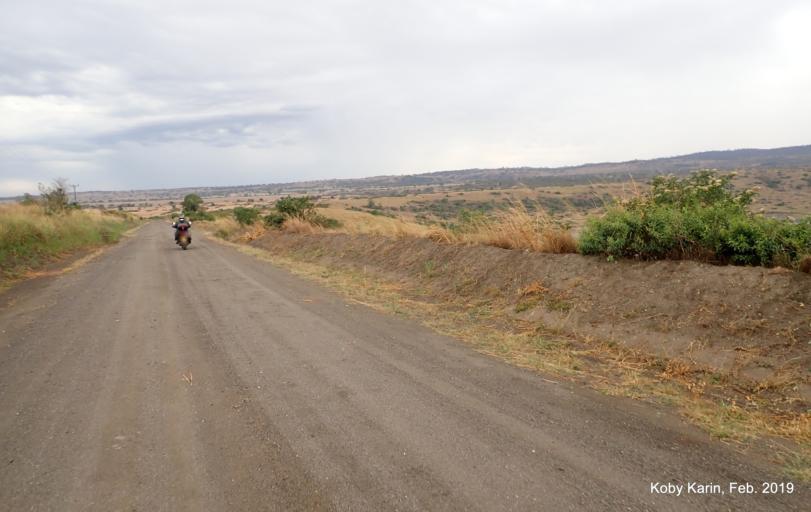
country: UG
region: Western Region
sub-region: Rubirizi District
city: Rubirizi
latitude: -0.0970
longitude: 29.9666
